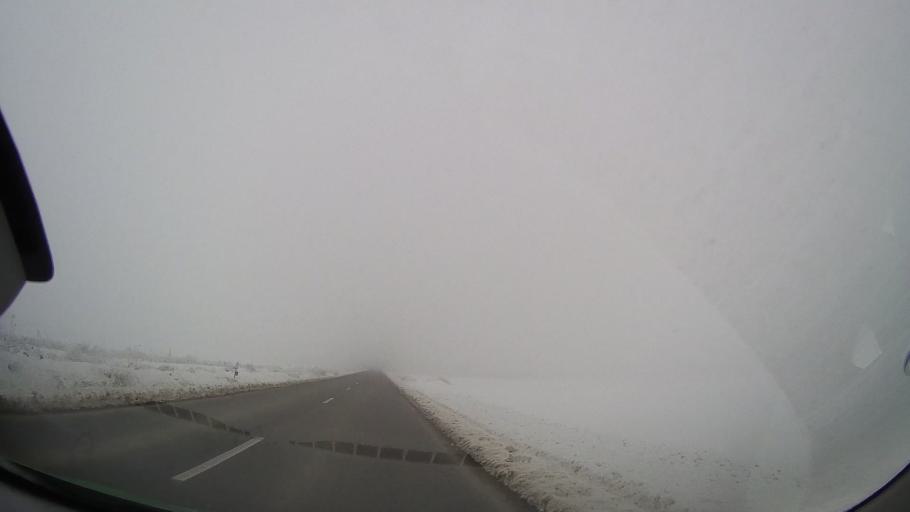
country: RO
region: Iasi
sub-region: Comuna Mogosesti-Siret
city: Mogosesti-Siret
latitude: 47.1547
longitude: 26.7768
